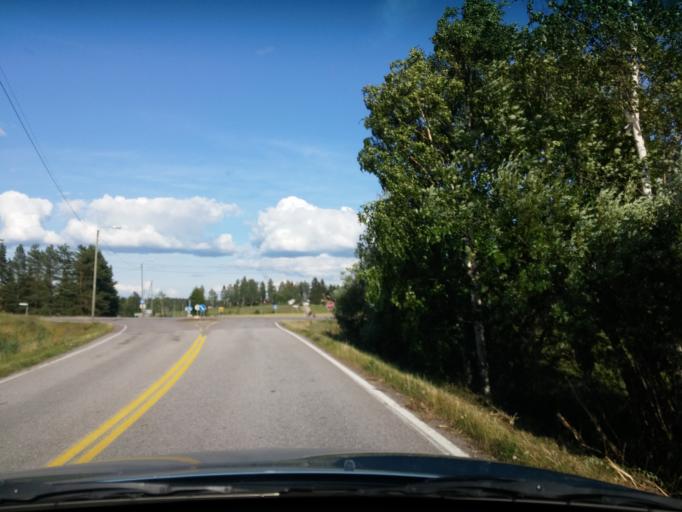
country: FI
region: Uusimaa
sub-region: Porvoo
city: Askola
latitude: 60.5253
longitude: 25.5797
